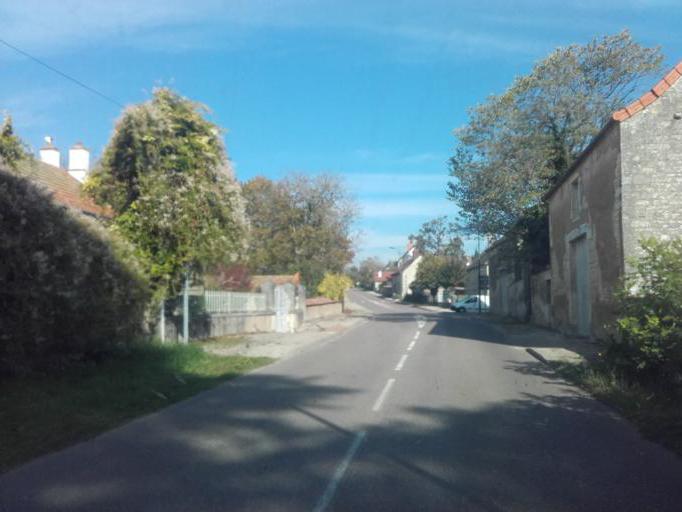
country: FR
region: Bourgogne
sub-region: Departement de Saone-et-Loire
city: Fontaines
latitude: 46.8490
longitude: 4.7543
